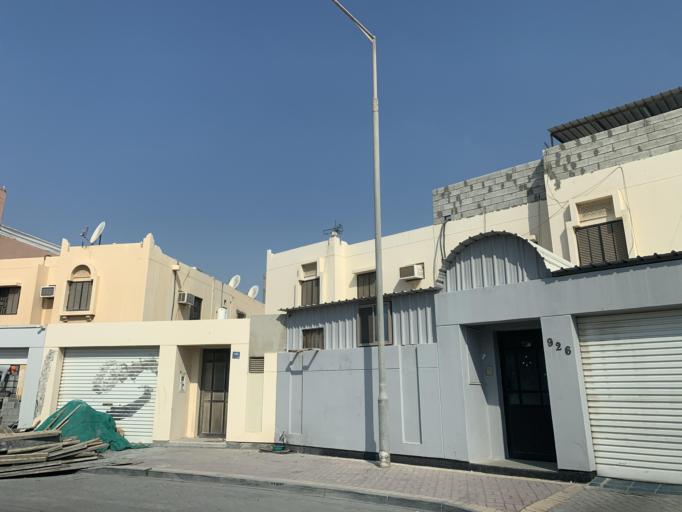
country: BH
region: Central Governorate
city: Madinat Hamad
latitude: 26.1110
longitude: 50.4998
